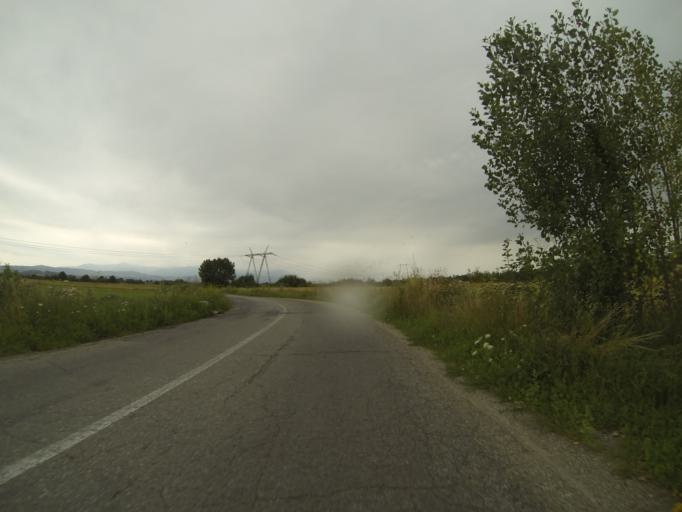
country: RO
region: Brasov
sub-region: Comuna Sinca Veche
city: Sinca Veche
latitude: 45.7824
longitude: 25.1478
